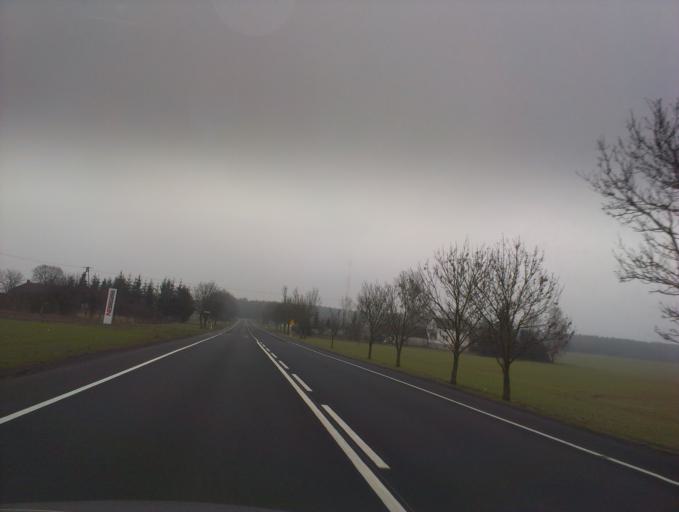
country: PL
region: Greater Poland Voivodeship
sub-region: Powiat pilski
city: Ujscie
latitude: 53.0342
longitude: 16.7790
